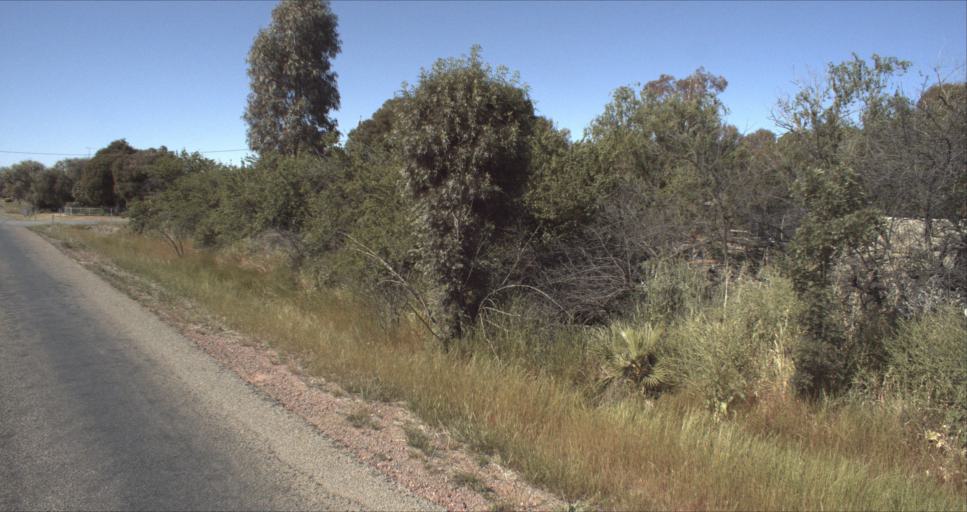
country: AU
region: New South Wales
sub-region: Leeton
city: Leeton
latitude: -34.5550
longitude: 146.3847
